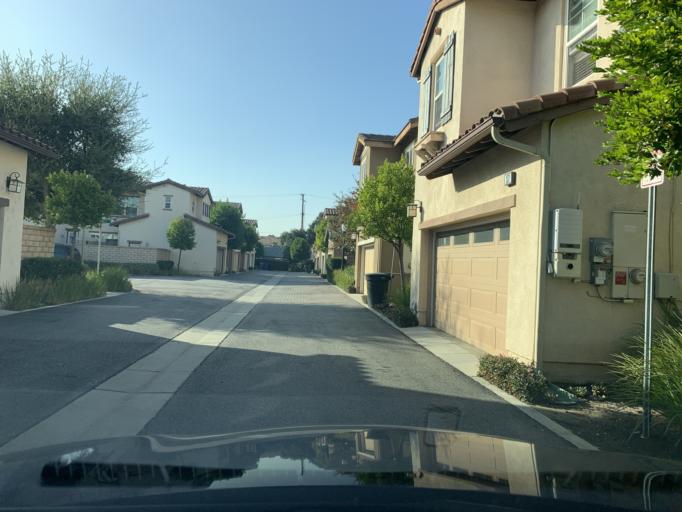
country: US
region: California
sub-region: Los Angeles County
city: Covina
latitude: 34.0836
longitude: -117.8912
